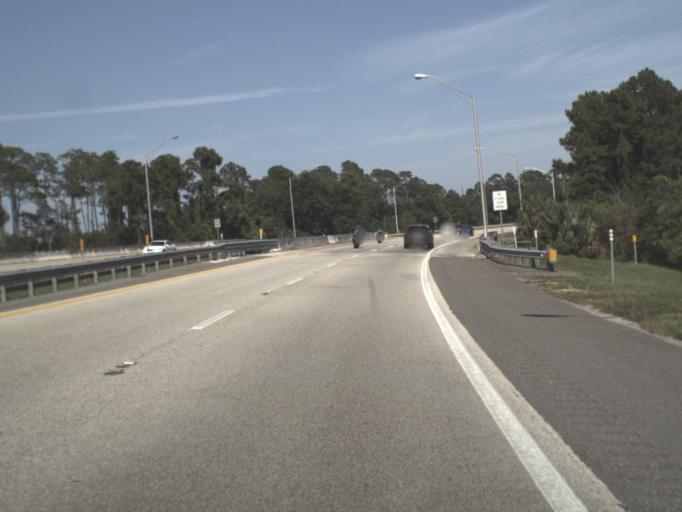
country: US
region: Florida
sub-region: Saint Johns County
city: Ponte Vedra Beach
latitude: 30.2591
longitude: -81.4089
